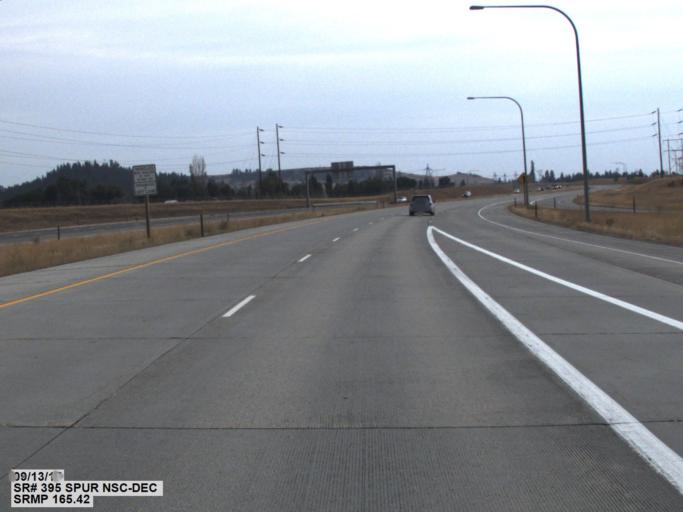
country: US
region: Washington
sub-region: Spokane County
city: Mead
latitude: 47.7690
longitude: -117.3678
